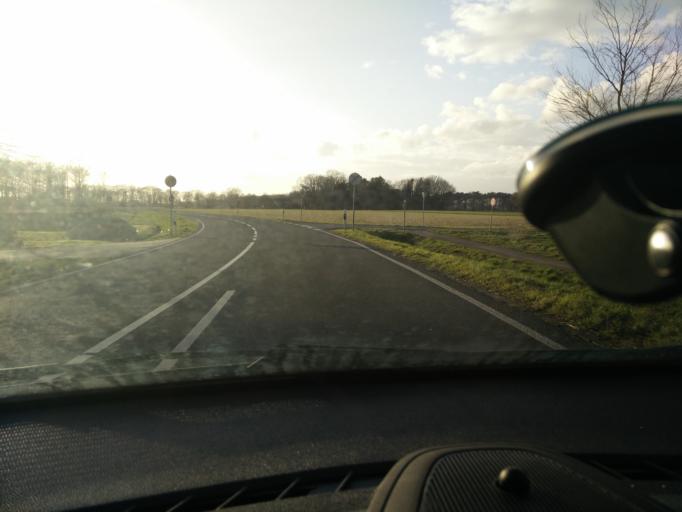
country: DE
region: North Rhine-Westphalia
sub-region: Regierungsbezirk Munster
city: Borken
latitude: 51.8094
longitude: 6.8862
